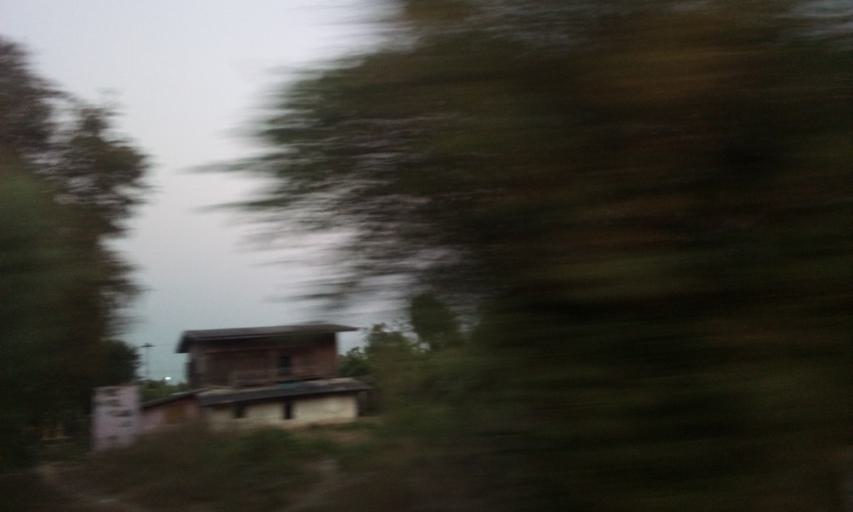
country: TH
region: Sing Buri
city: Phrom Buri
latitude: 14.8241
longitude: 100.4073
